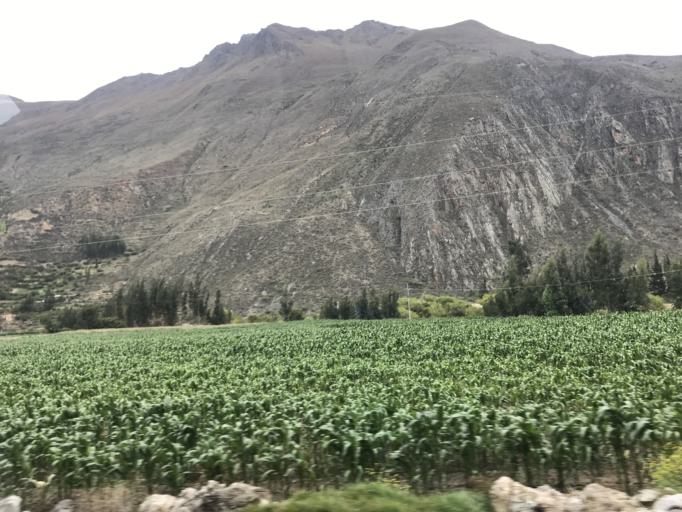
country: PE
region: Cusco
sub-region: Provincia de Urubamba
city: Ollantaytambo
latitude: -13.2443
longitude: -72.2939
